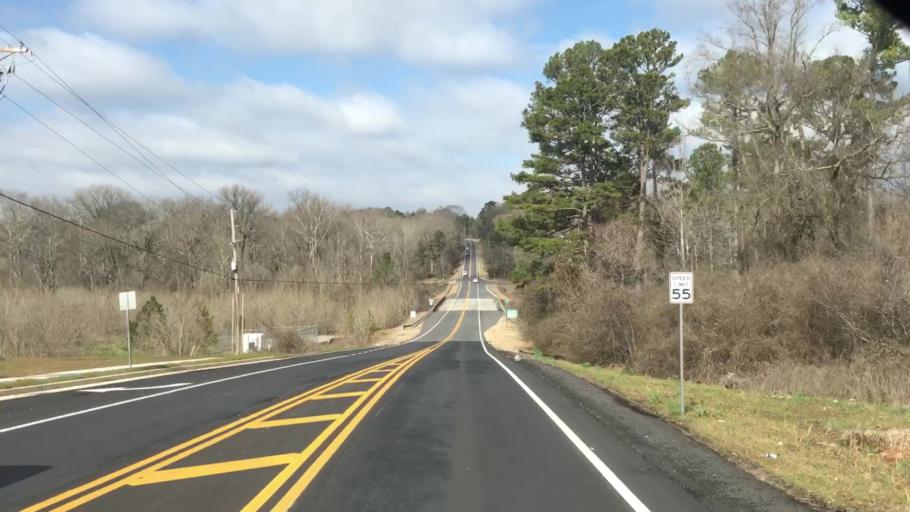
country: US
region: Georgia
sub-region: Jackson County
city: Braselton
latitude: 34.1277
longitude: -83.8303
